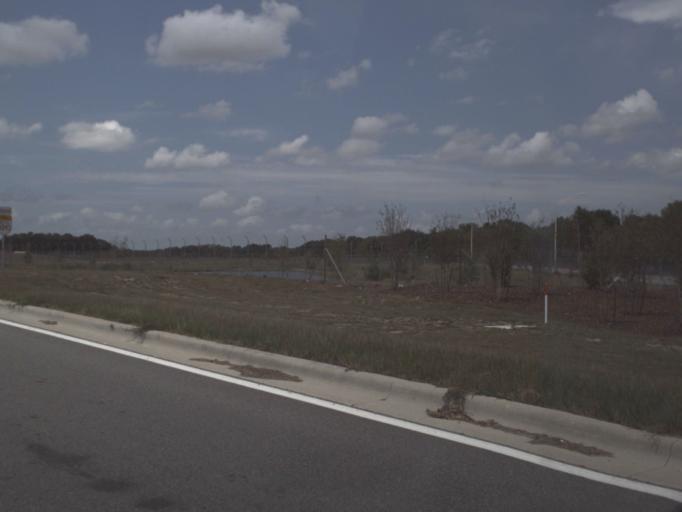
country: US
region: Florida
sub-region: Lake County
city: Mount Plymouth
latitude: 28.8122
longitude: -81.5053
